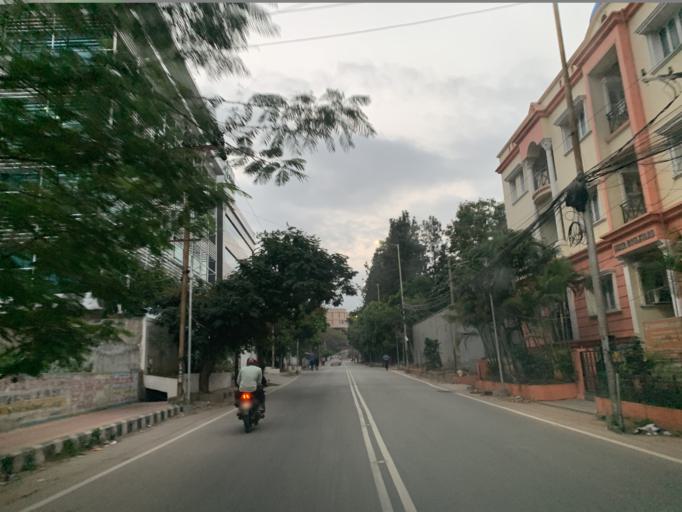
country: IN
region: Telangana
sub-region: Rangareddi
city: Kukatpalli
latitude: 17.4368
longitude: 78.3957
